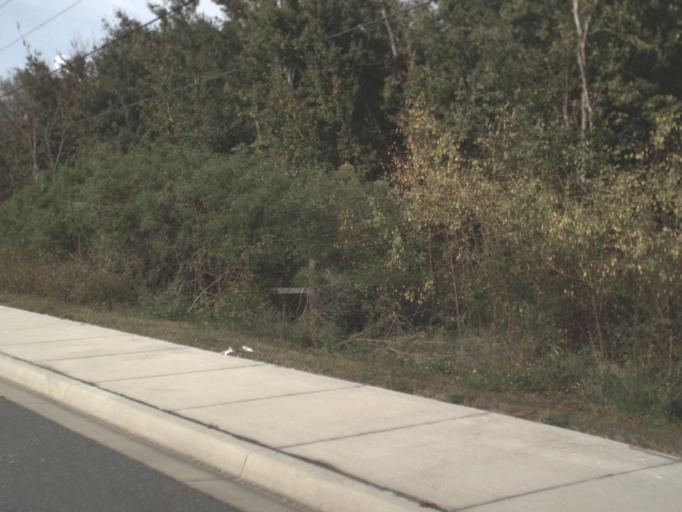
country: US
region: Florida
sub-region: Osceola County
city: Saint Cloud
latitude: 28.3472
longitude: -81.2309
